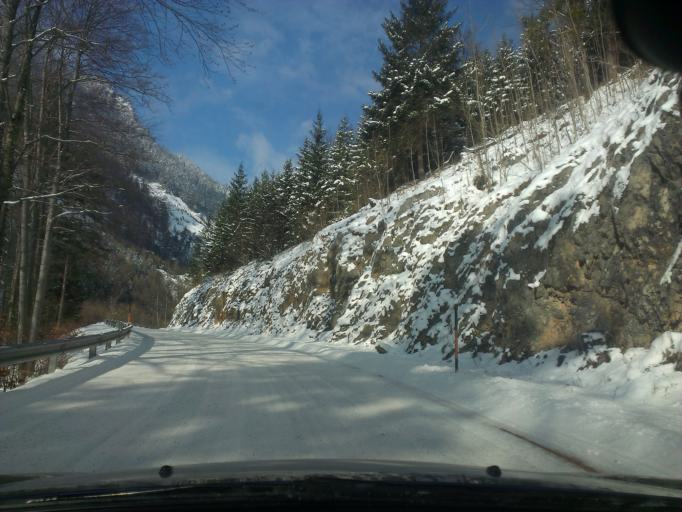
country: AT
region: Lower Austria
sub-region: Politischer Bezirk Neunkirchen
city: Reichenau an der Rax
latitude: 47.7420
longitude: 15.7808
